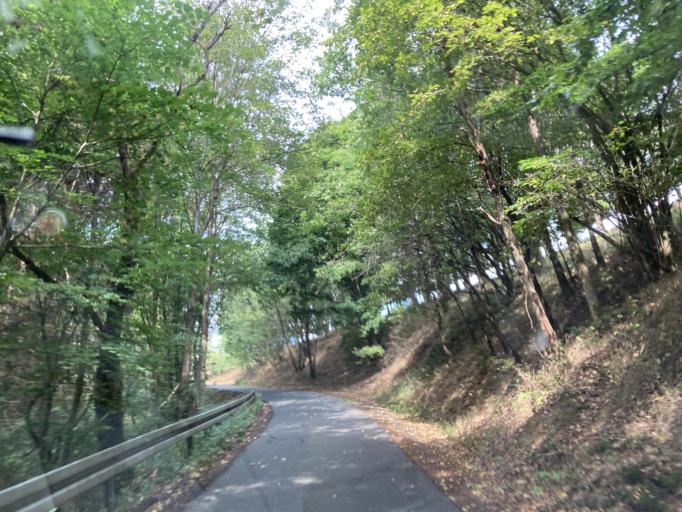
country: DE
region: Bavaria
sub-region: Upper Franconia
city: Grafengehaig
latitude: 50.1805
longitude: 11.5670
